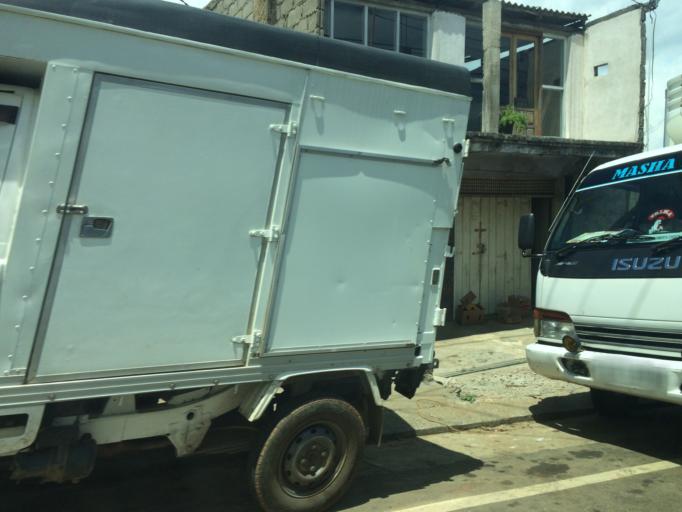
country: LK
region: Central
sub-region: Nuwara Eliya District
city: Nuwara Eliya
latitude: 6.9081
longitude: 80.8405
